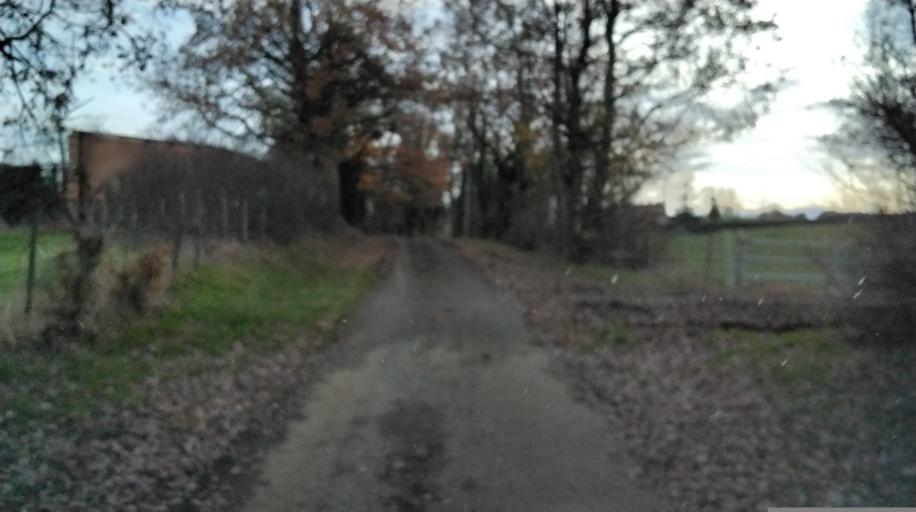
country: FR
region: Midi-Pyrenees
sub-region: Departement de la Haute-Garonne
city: Le Fousseret
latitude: 43.3008
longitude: 0.9824
